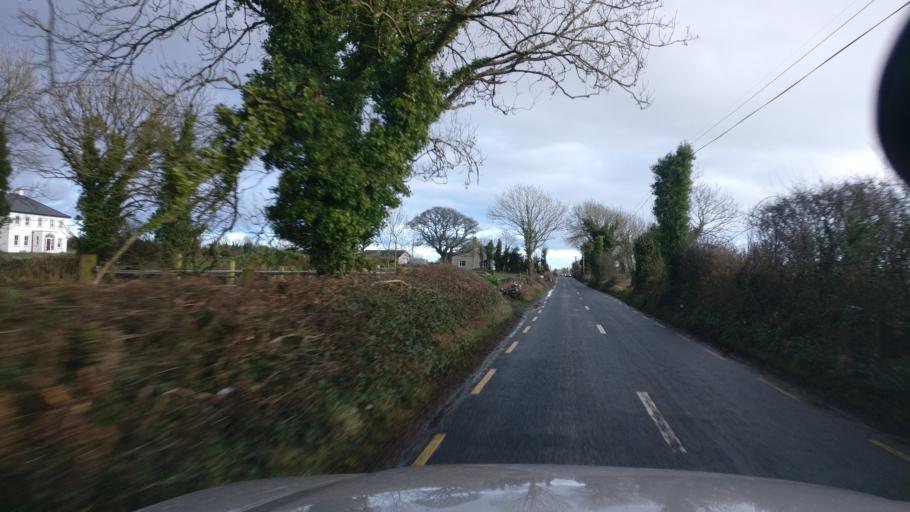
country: IE
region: Connaught
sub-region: County Galway
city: Athenry
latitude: 53.2923
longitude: -8.6415
